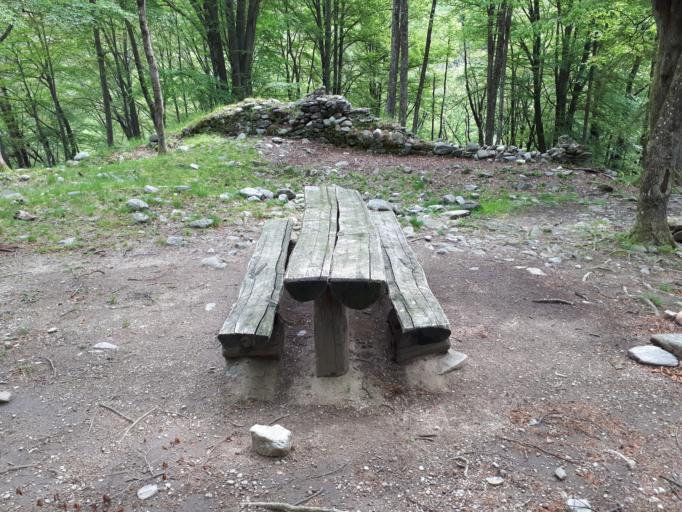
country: CH
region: Ticino
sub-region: Lugano District
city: Pura
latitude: 46.0193
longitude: 8.8643
